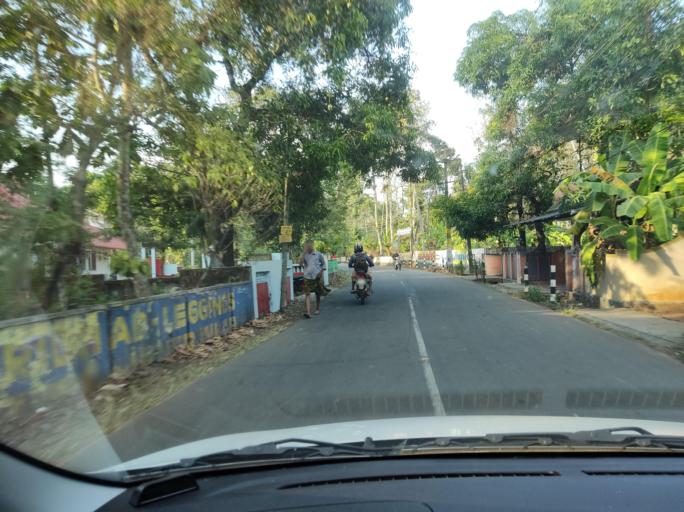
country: IN
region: Kerala
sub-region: Kottayam
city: Kottayam
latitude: 9.6569
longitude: 76.5064
